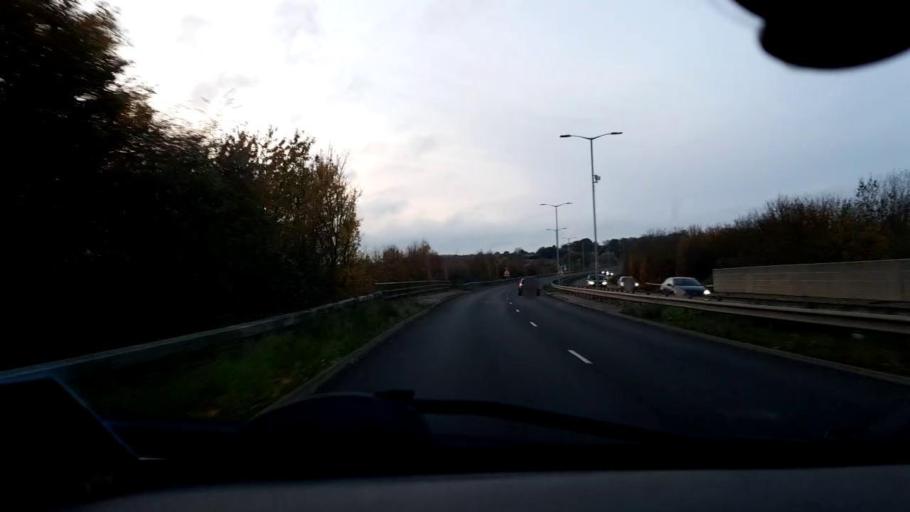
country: GB
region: England
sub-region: Norfolk
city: Thorpe Hamlet
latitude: 52.6088
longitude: 1.3136
